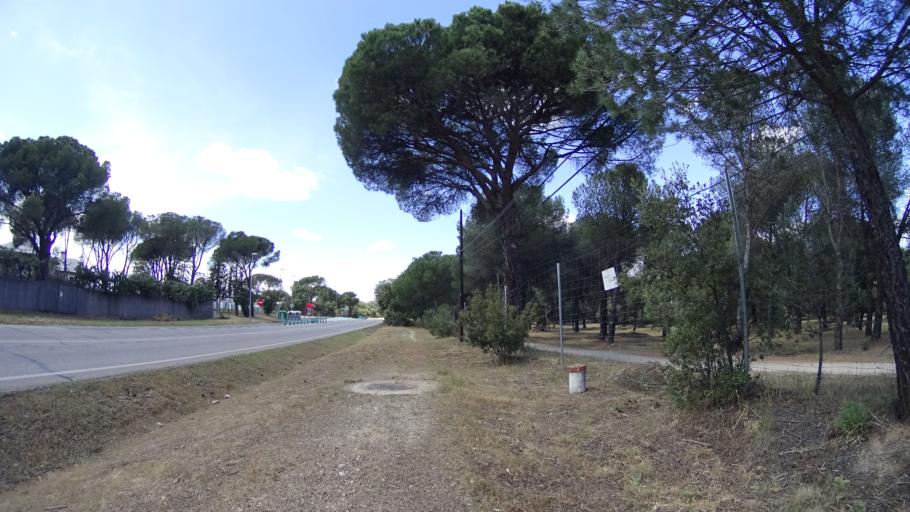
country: ES
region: Madrid
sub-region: Provincia de Madrid
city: Boadilla del Monte
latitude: 40.4331
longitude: -3.8724
